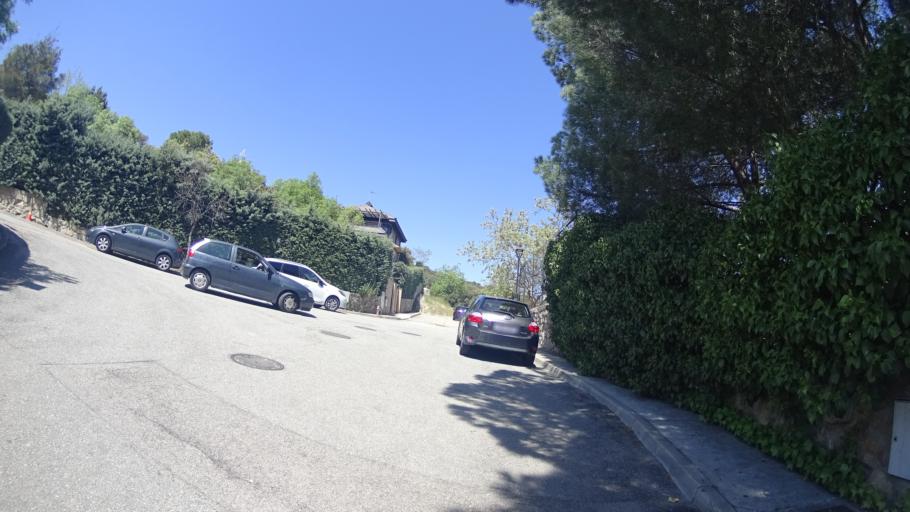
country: ES
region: Madrid
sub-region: Provincia de Madrid
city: Galapagar
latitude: 40.5866
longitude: -3.9709
